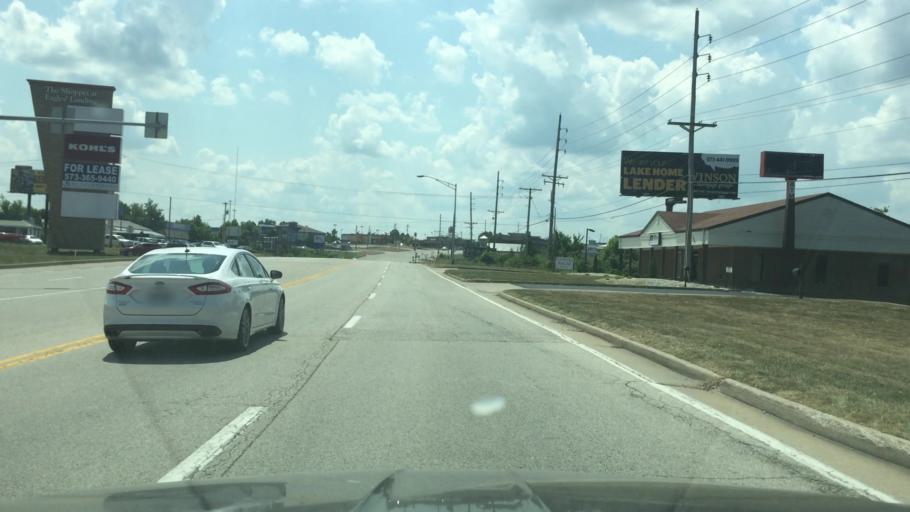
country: US
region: Missouri
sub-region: Miller County
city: Lake Ozark
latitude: 38.1735
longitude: -92.6146
